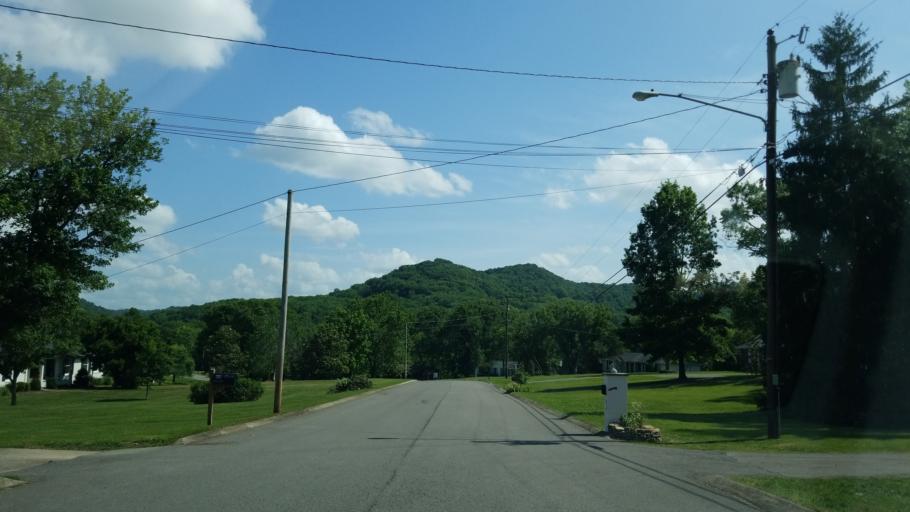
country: US
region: Tennessee
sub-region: Davidson County
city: Forest Hills
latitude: 36.0289
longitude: -86.8516
